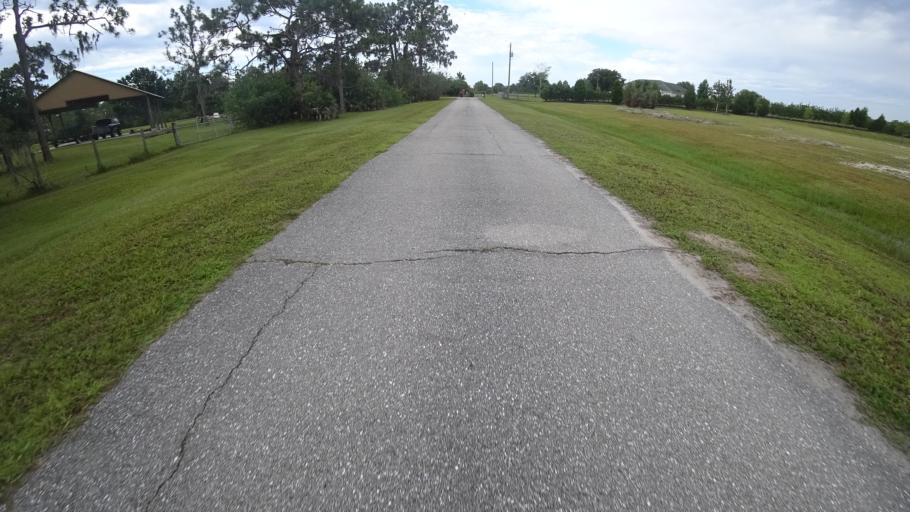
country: US
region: Florida
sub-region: Sarasota County
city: The Meadows
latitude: 27.4222
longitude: -82.2791
